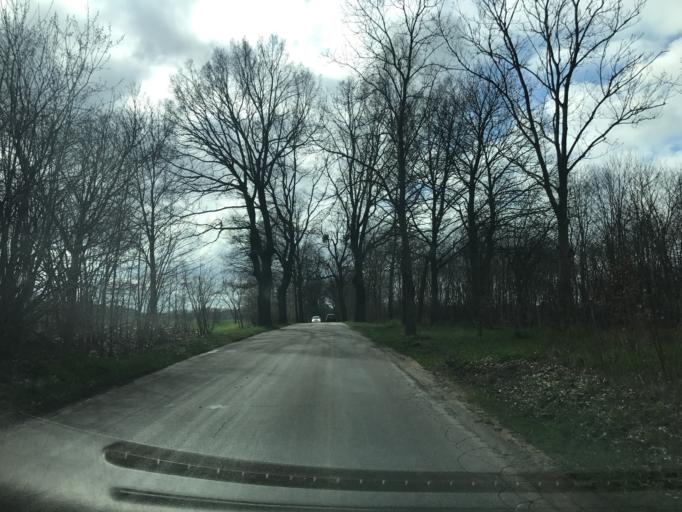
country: PL
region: Warmian-Masurian Voivodeship
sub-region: Powiat ostrodzki
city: Gierzwald
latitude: 53.4850
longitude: 20.1004
